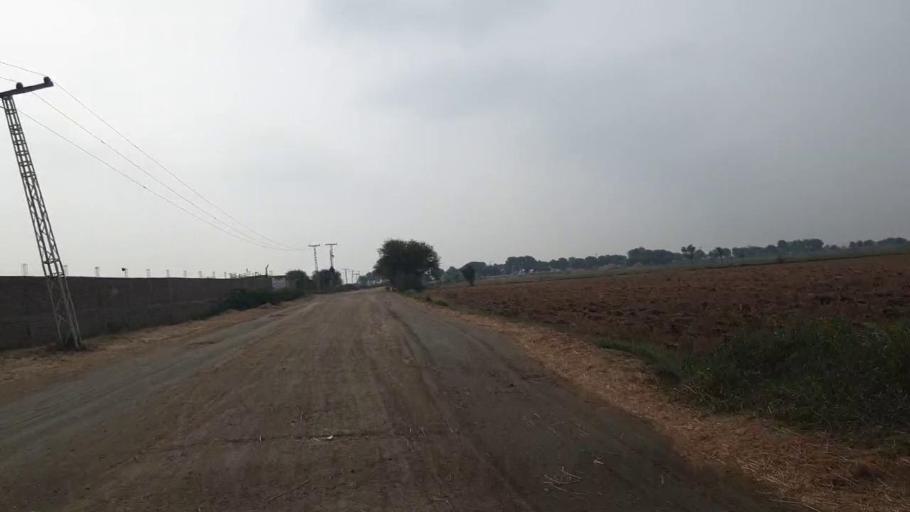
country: PK
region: Sindh
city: Matli
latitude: 24.9381
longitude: 68.5753
